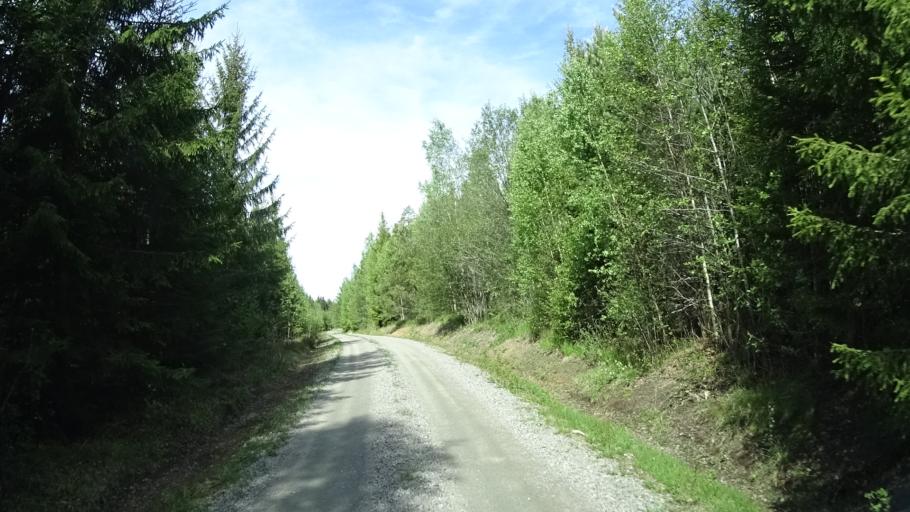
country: SE
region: OEstergoetland
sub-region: Finspangs Kommun
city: Finspang
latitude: 58.7940
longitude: 15.8586
